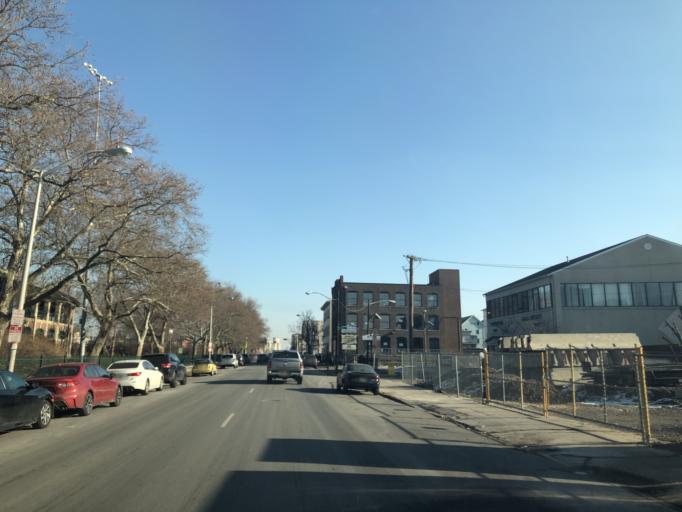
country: US
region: New Jersey
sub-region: Hudson County
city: Harrison
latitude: 40.7316
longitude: -74.1543
